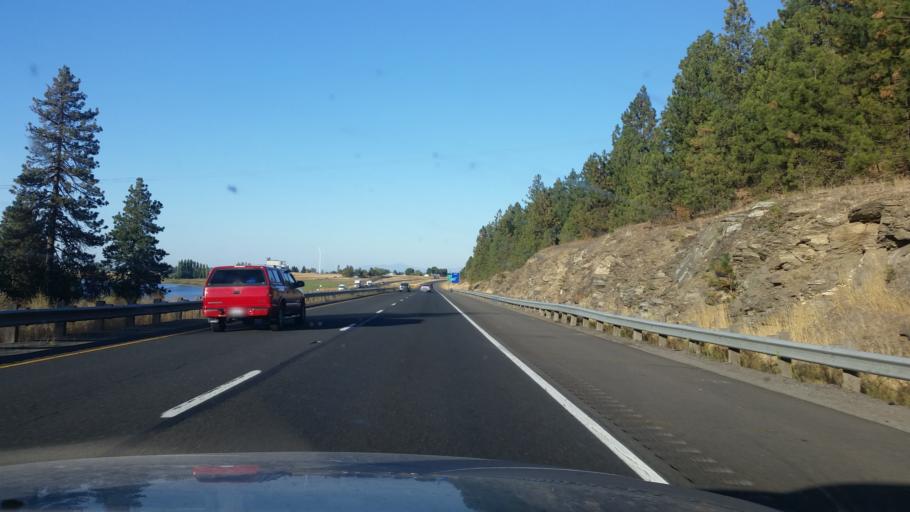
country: US
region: Washington
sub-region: Spokane County
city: Medical Lake
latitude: 47.5520
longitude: -117.6203
